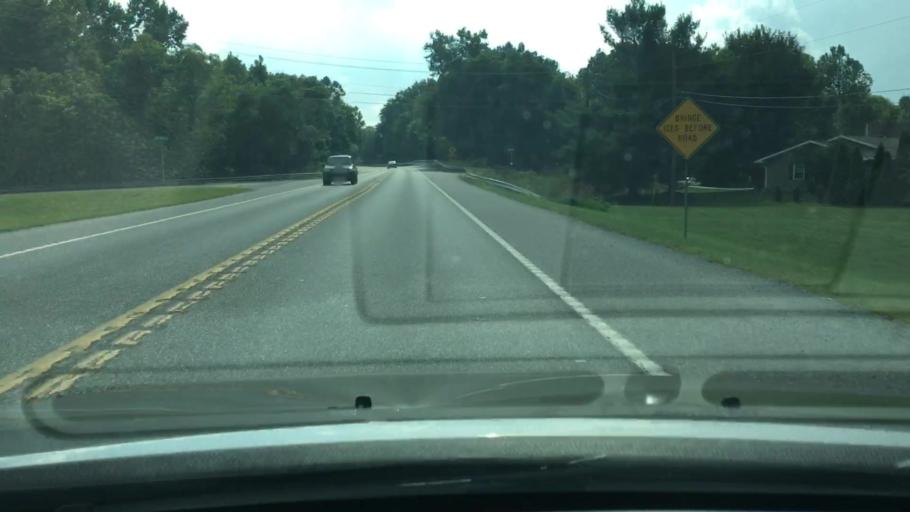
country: US
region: Pennsylvania
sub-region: Franklin County
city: Guilford
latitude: 39.9392
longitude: -77.5876
